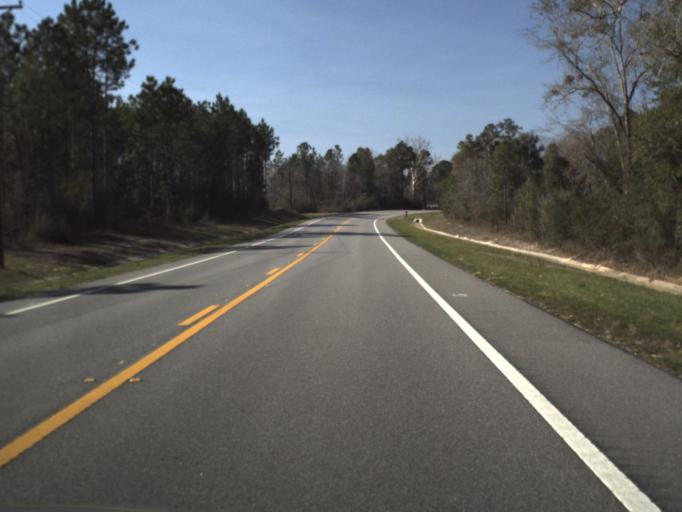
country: US
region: Florida
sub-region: Gulf County
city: Wewahitchka
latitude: 30.2496
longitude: -85.2281
